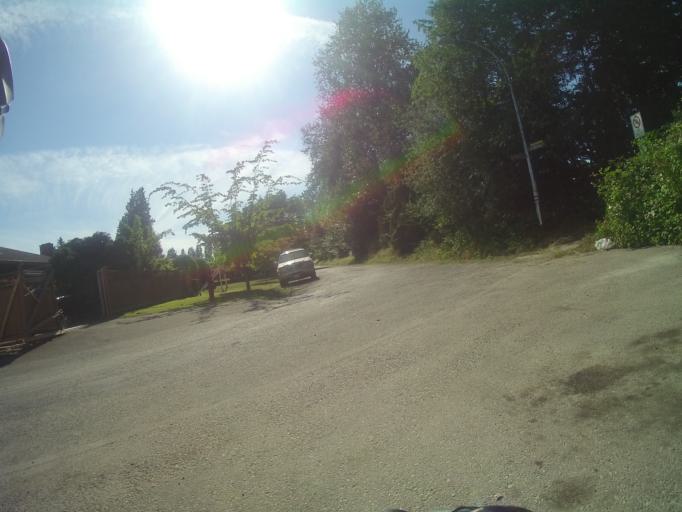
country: CA
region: British Columbia
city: Vancouver
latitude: 49.2178
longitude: -123.1131
